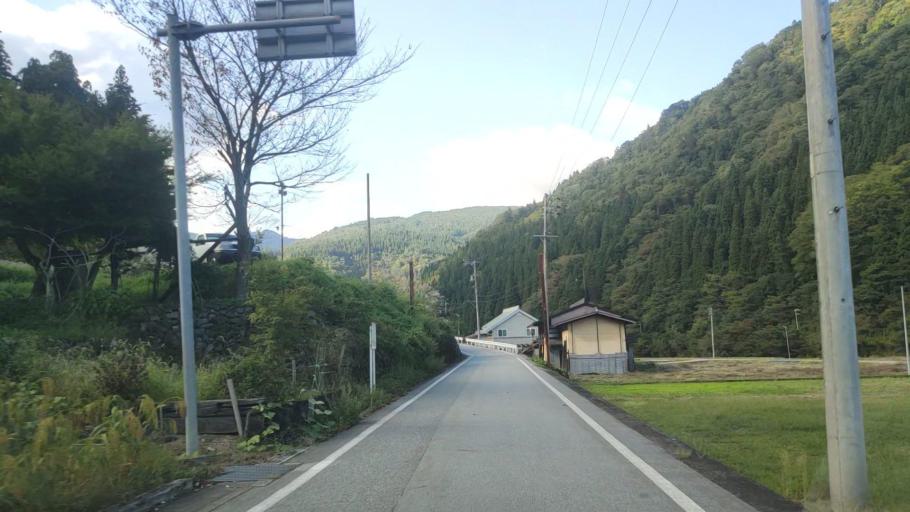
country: JP
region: Gifu
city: Takayama
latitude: 36.2987
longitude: 137.1143
